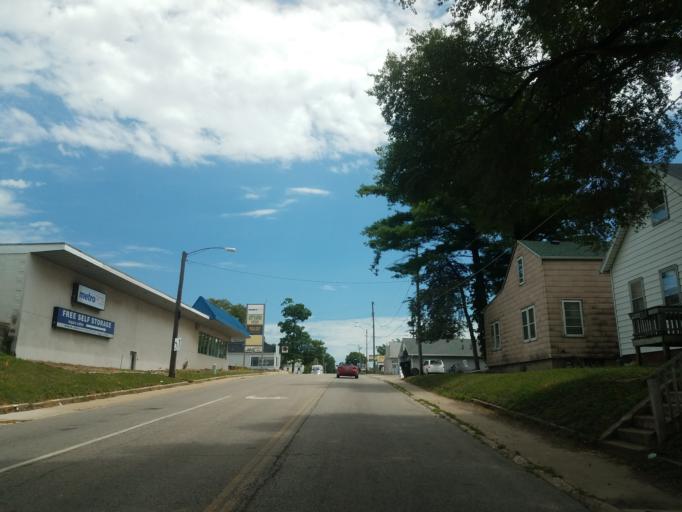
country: US
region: Illinois
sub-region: McLean County
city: Bloomington
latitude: 40.4821
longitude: -89.0059
